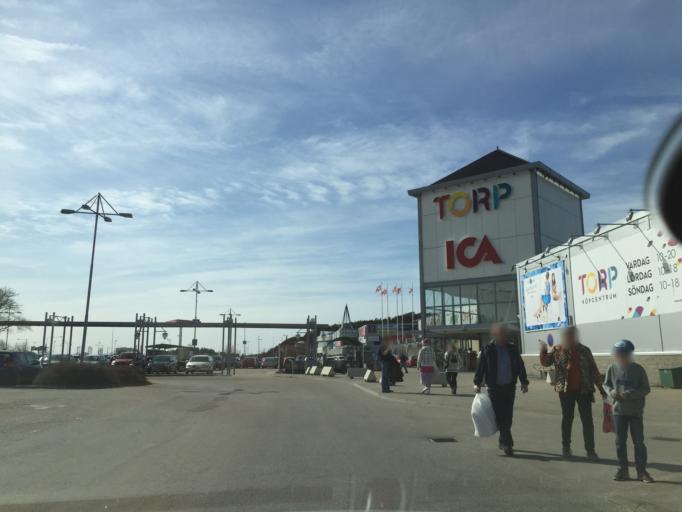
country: SE
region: Vaestra Goetaland
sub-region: Uddevalla Kommun
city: Uddevalla
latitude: 58.3537
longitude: 11.8101
